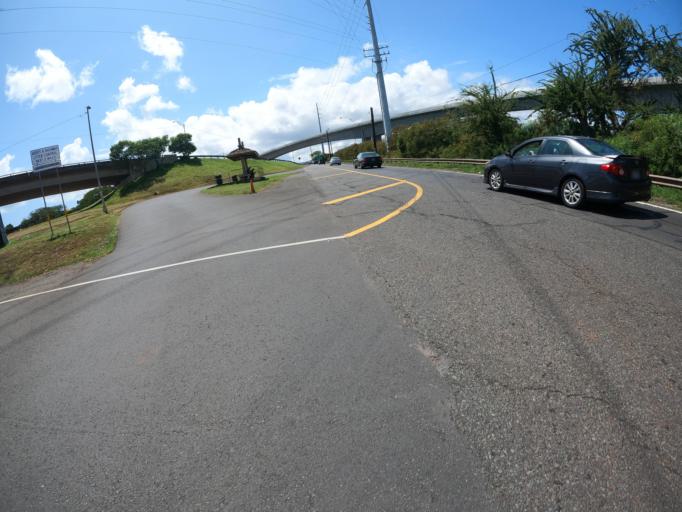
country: US
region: Hawaii
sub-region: Honolulu County
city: Pearl City, Manana
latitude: 21.3966
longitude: -157.9815
